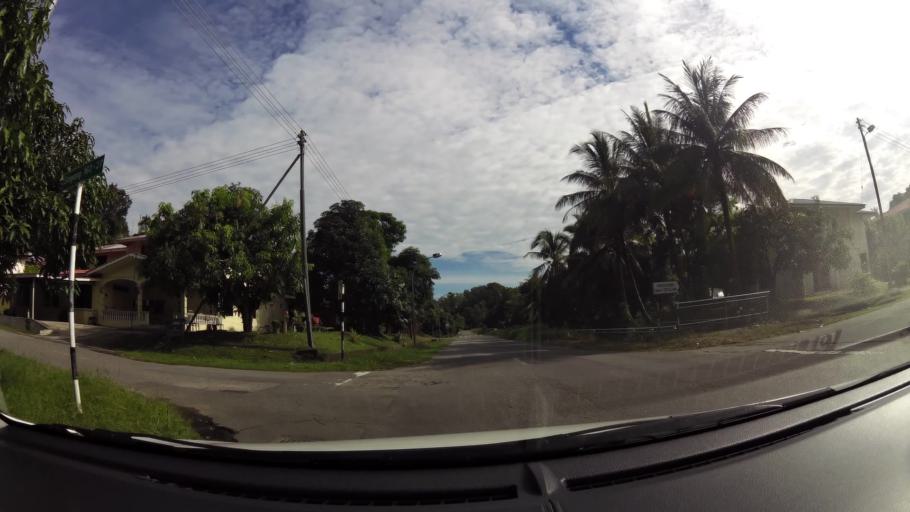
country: BN
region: Brunei and Muara
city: Bandar Seri Begawan
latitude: 4.9197
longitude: 114.8970
